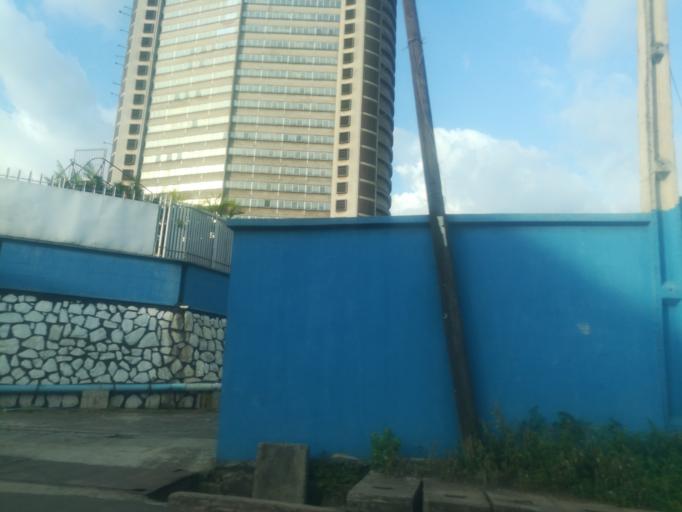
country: NG
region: Oyo
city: Ibadan
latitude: 7.3871
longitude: 3.8787
